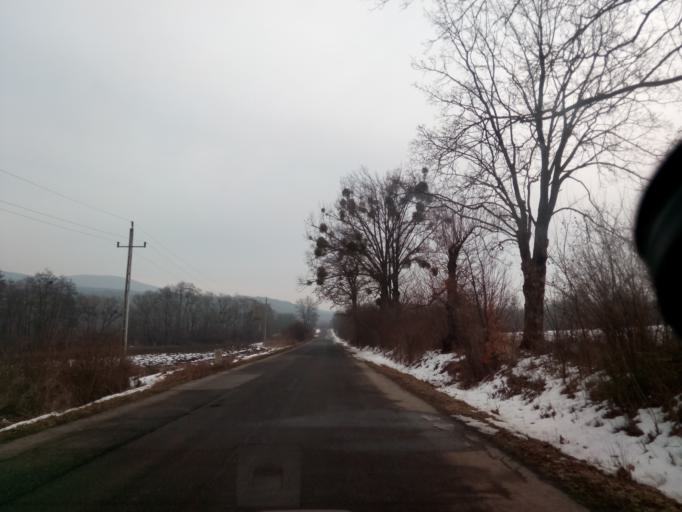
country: HU
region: Borsod-Abauj-Zemplen
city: Gonc
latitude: 48.5064
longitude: 21.3219
